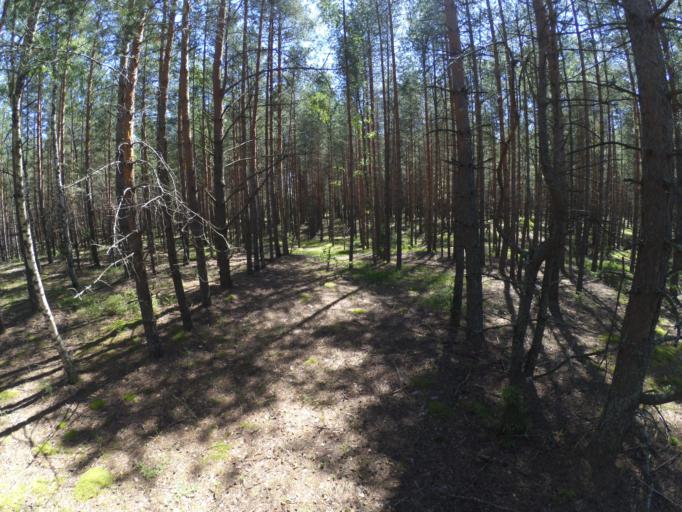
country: RU
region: Moskovskaya
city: Fosforitnyy
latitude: 55.3432
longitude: 38.9198
